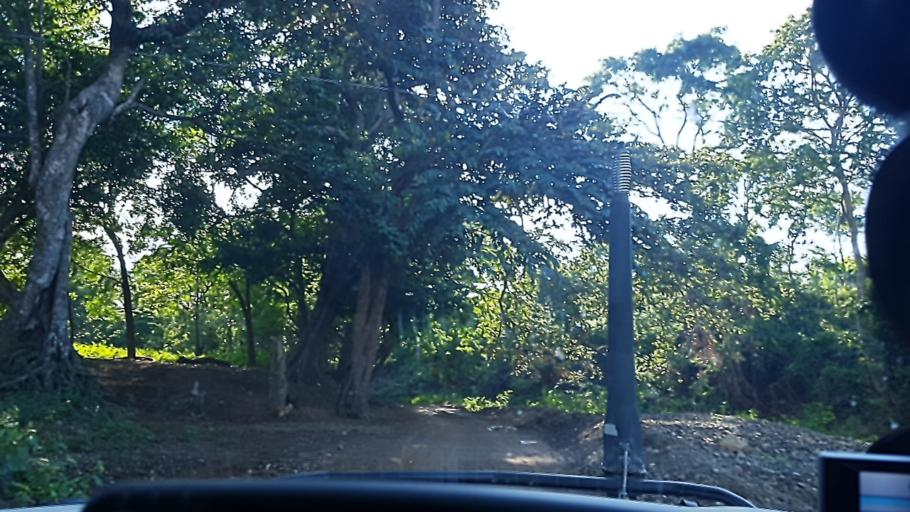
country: NI
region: Rivas
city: Tola
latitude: 11.5364
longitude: -86.1316
